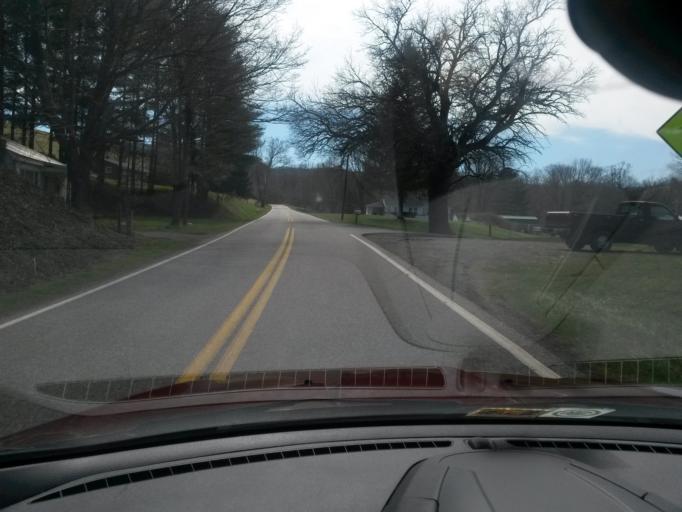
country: US
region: West Virginia
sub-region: Greenbrier County
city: White Sulphur Springs
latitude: 37.6452
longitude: -80.2377
